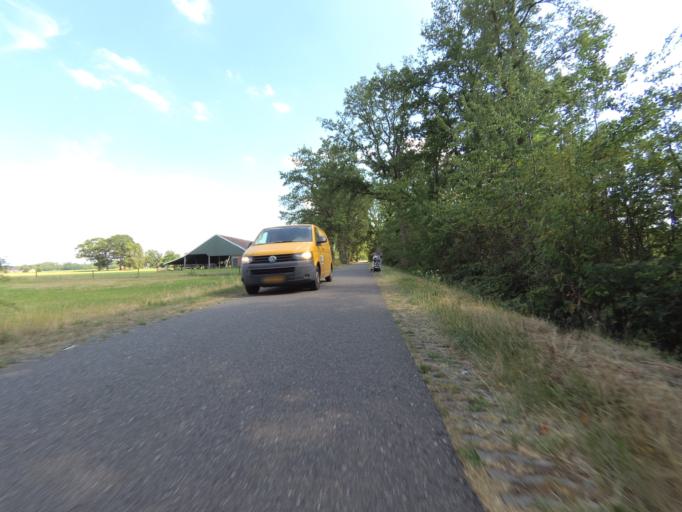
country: NL
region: Overijssel
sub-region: Gemeente Oldenzaal
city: Oldenzaal
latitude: 52.3326
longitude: 6.9150
